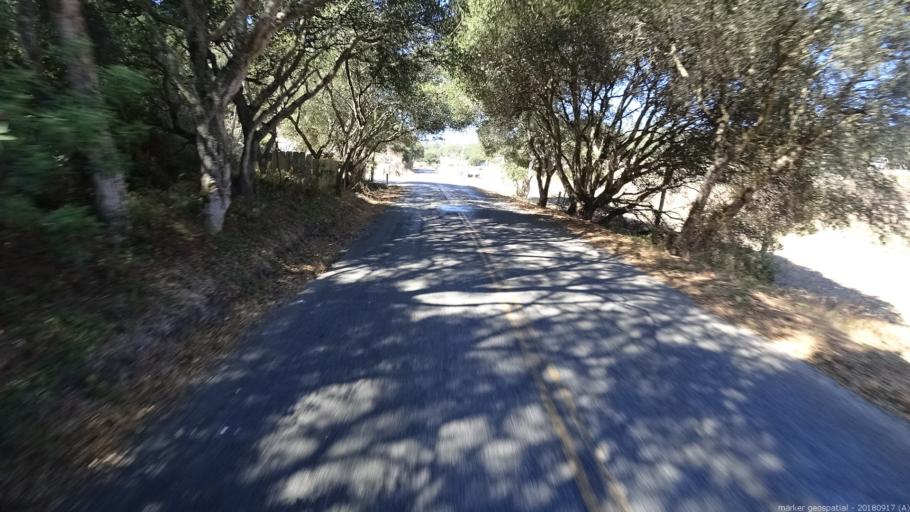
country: US
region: California
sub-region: Monterey County
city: Elkhorn
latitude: 36.8386
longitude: -121.7185
